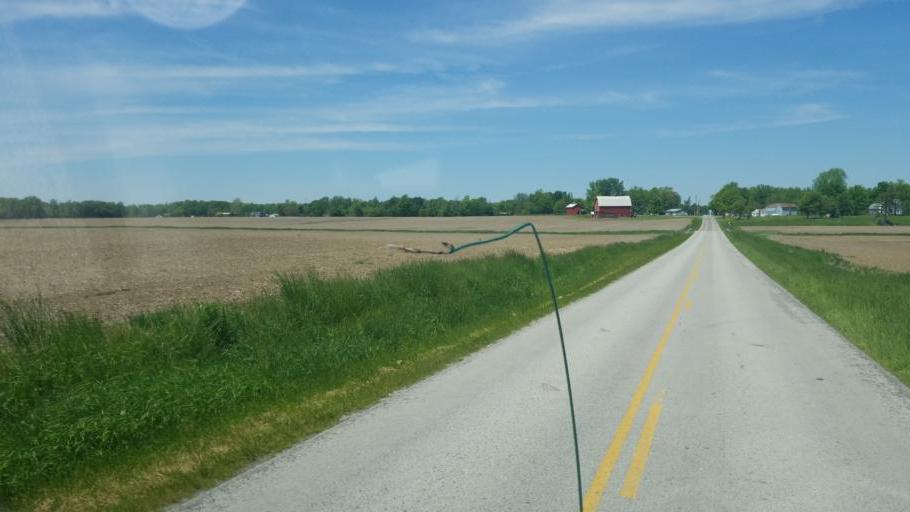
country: US
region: Ohio
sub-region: Huron County
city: Greenwich
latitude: 41.1479
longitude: -82.5385
